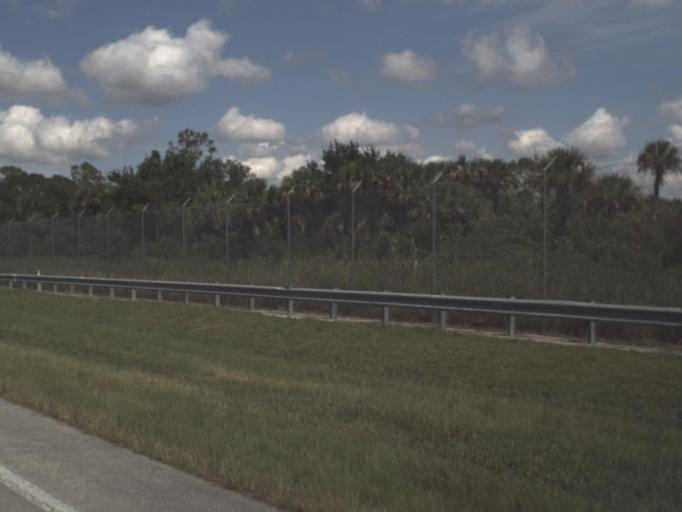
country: US
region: Florida
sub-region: Collier County
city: Immokalee
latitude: 26.1638
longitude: -81.3452
